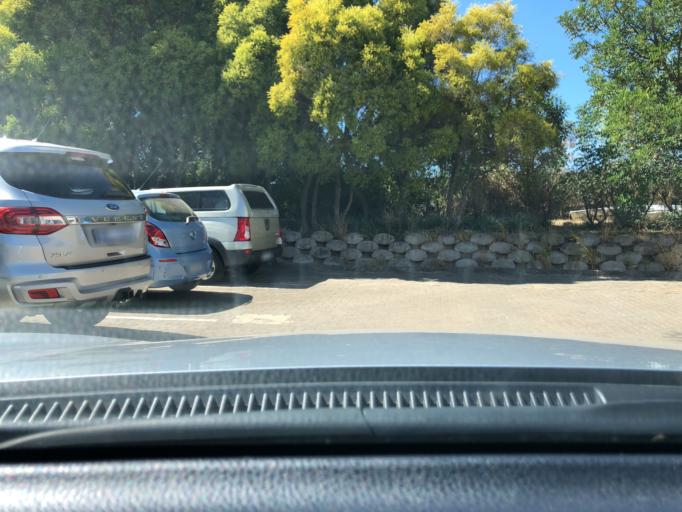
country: ZA
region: KwaZulu-Natal
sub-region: Amajuba District Municipality
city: Newcastle
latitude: -27.7607
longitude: 30.0248
